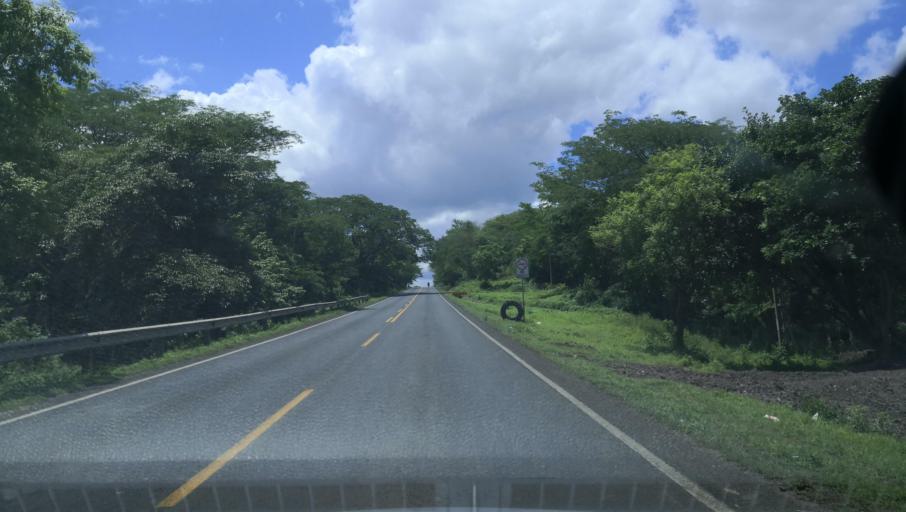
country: NI
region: Esteli
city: Condega
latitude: 13.3849
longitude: -86.4014
